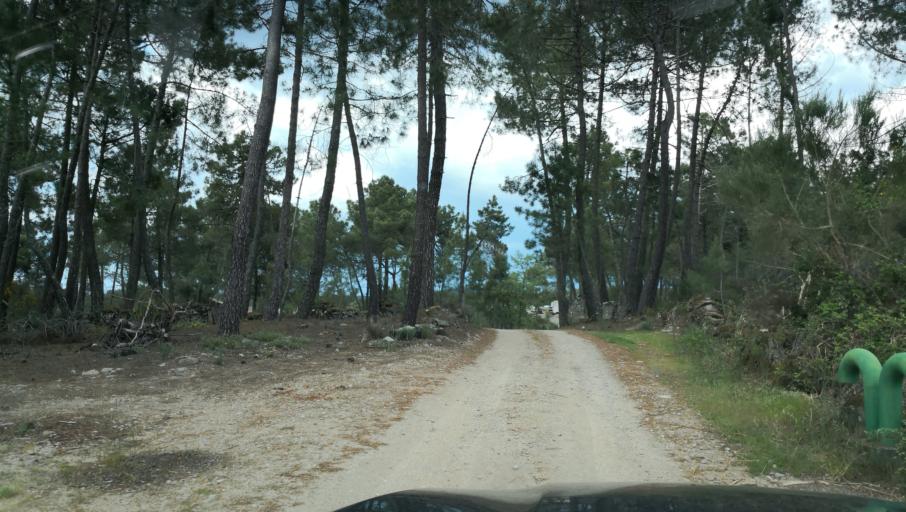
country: PT
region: Vila Real
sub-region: Vila Real
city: Vila Real
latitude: 41.2990
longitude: -7.6872
